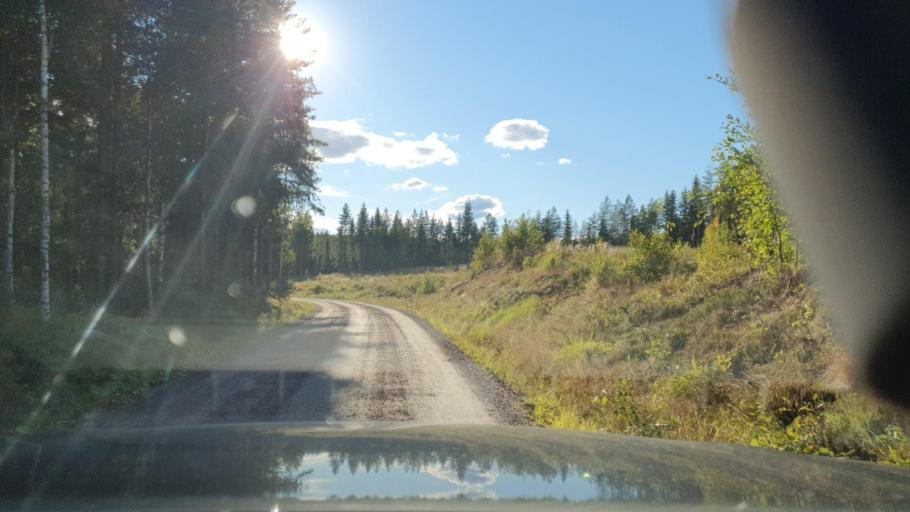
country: SE
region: Vaermland
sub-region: Karlstads Kommun
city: Molkom
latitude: 59.6483
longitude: 13.8654
